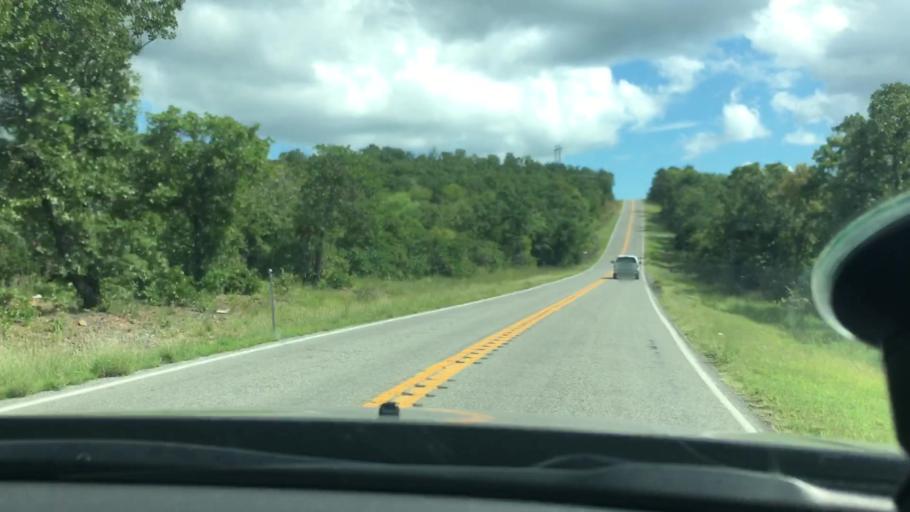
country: US
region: Oklahoma
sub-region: Sequoyah County
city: Vian
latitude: 35.6266
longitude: -94.9636
